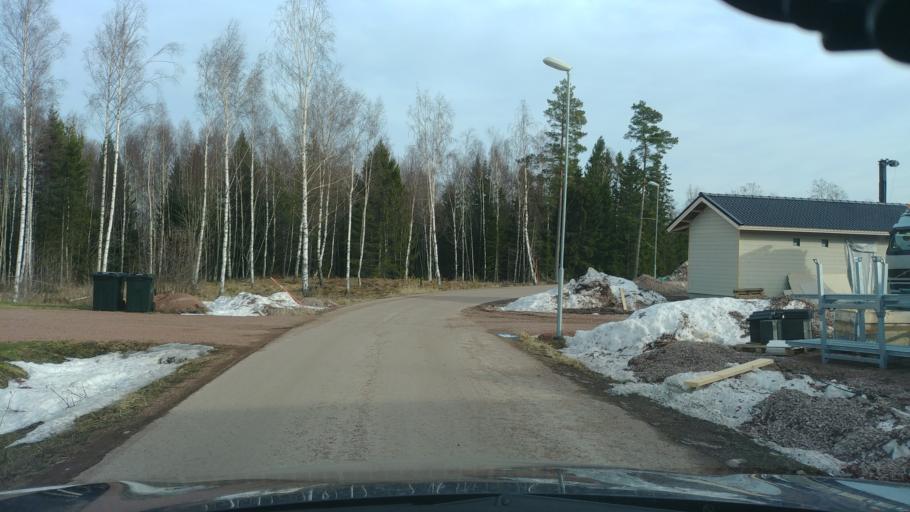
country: AX
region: Mariehamns stad
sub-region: Mariehamn
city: Mariehamn
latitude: 60.0998
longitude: 19.8952
